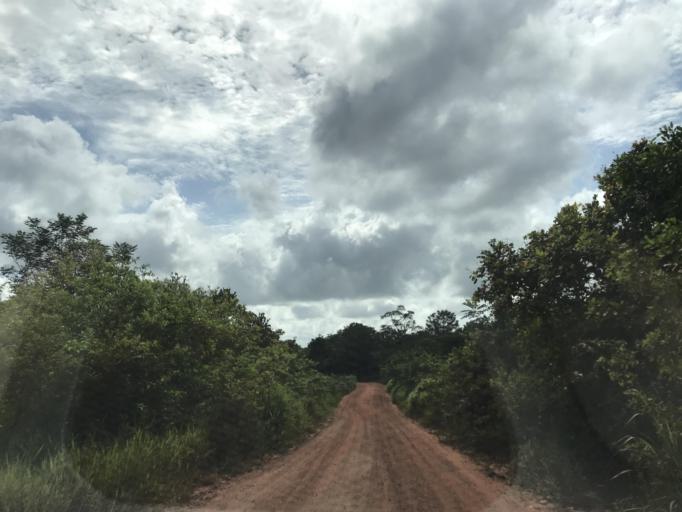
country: BR
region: Bahia
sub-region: Entre Rios
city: Entre Rios
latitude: -12.1706
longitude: -38.1503
